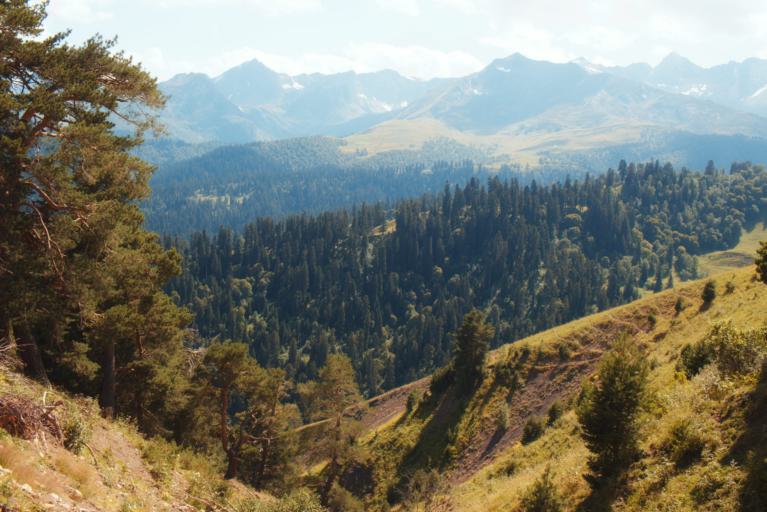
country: RU
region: Karachayevo-Cherkesiya
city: Mednogorskiy
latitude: 43.5830
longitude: 41.0935
